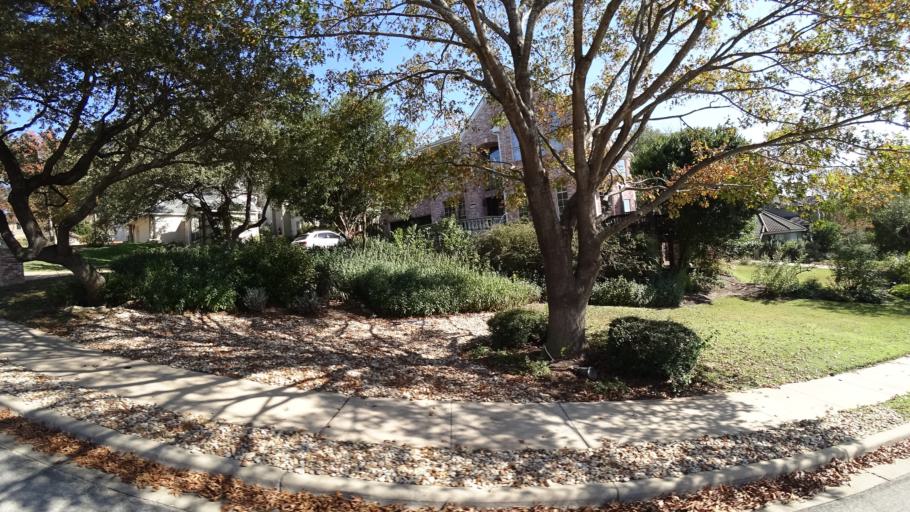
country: US
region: Texas
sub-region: Travis County
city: Lost Creek
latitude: 30.3666
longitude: -97.8632
